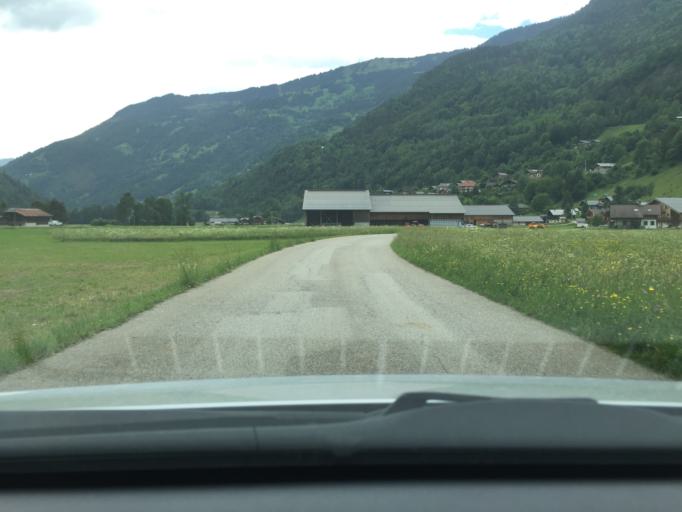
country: FR
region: Rhone-Alpes
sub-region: Departement de la Savoie
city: Beaufort
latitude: 45.7228
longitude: 6.5584
